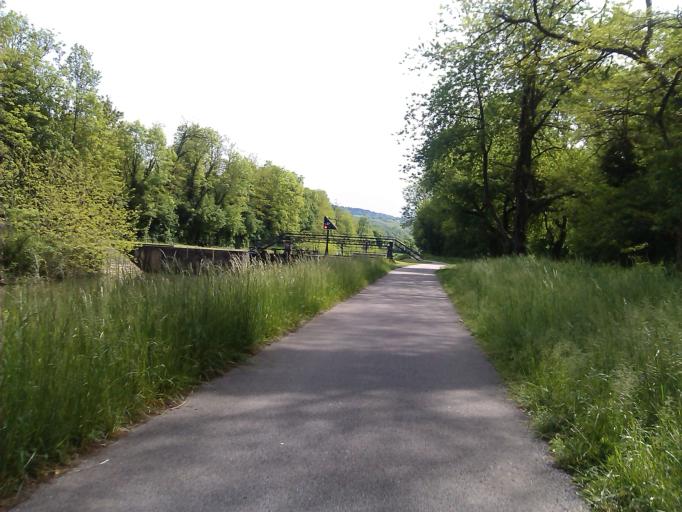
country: FR
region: Franche-Comte
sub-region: Departement du Doubs
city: Boussieres
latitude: 47.1538
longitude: 5.8835
